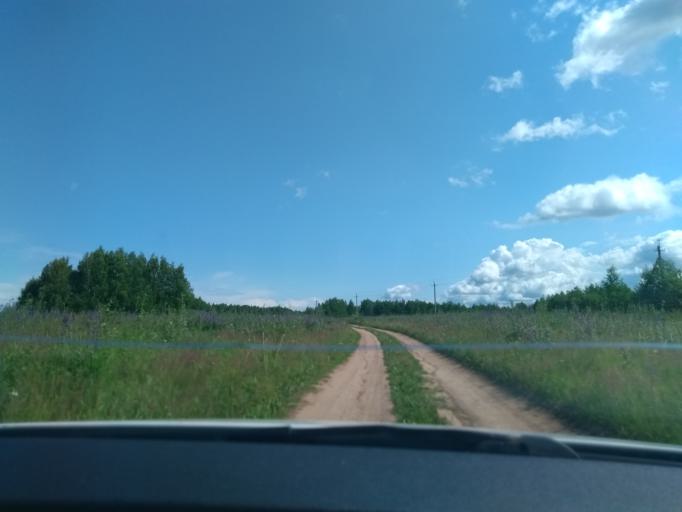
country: RU
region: Perm
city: Sylva
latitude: 57.8231
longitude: 56.7450
